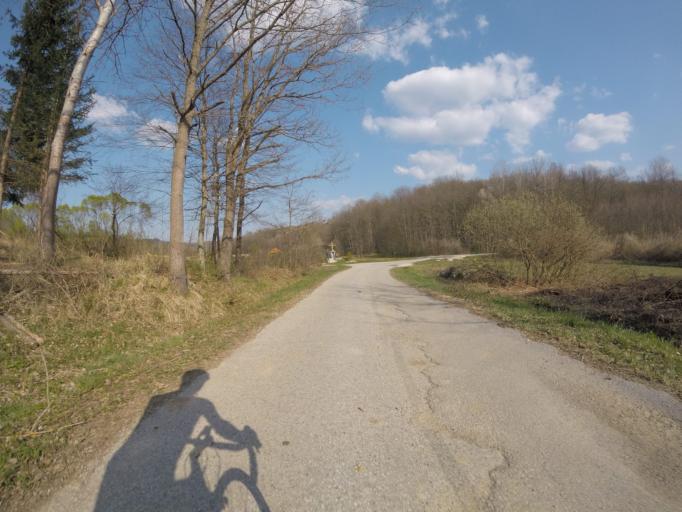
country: HR
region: Sisacko-Moslavacka
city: Glina
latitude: 45.5035
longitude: 16.0078
